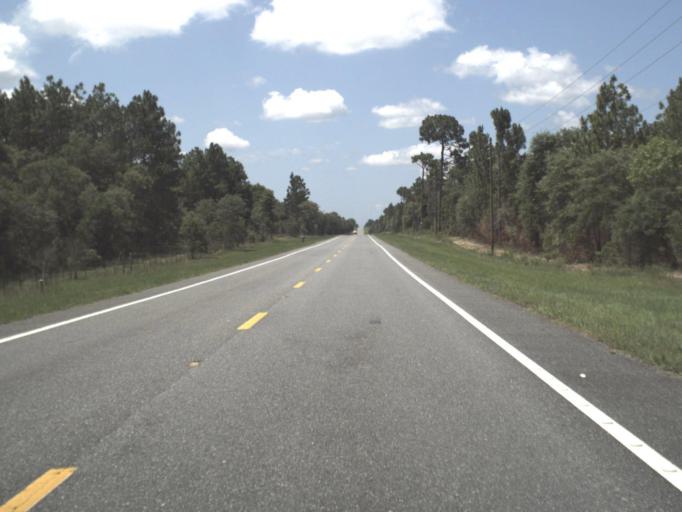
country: US
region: Florida
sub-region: Levy County
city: Williston Highlands
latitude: 29.2687
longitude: -82.5448
